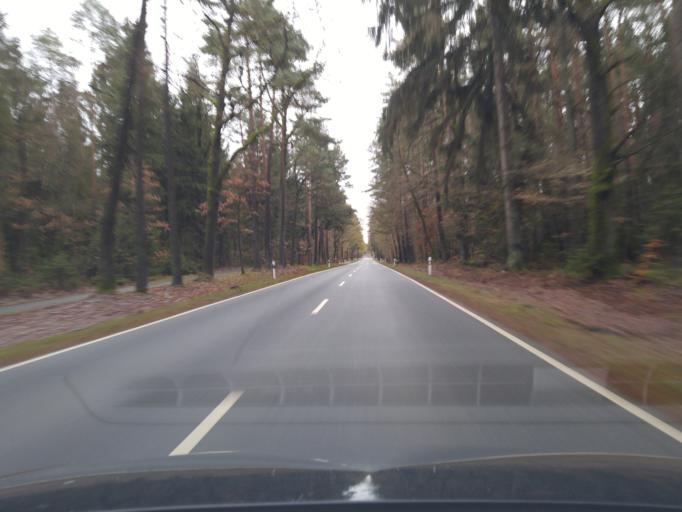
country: DE
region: Lower Saxony
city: Winsen (Aller)
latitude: 52.7476
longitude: 9.9177
